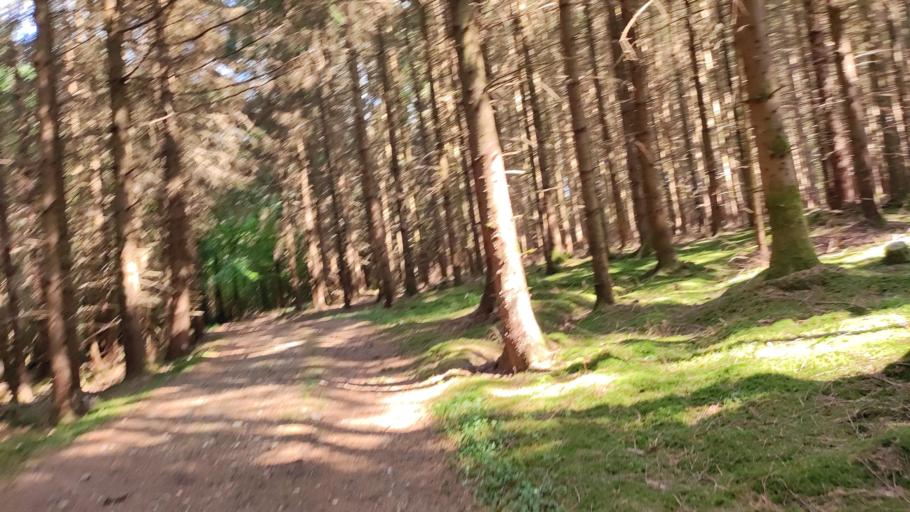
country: DE
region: Bavaria
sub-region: Swabia
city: Dinkelscherben
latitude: 48.3687
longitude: 10.6008
